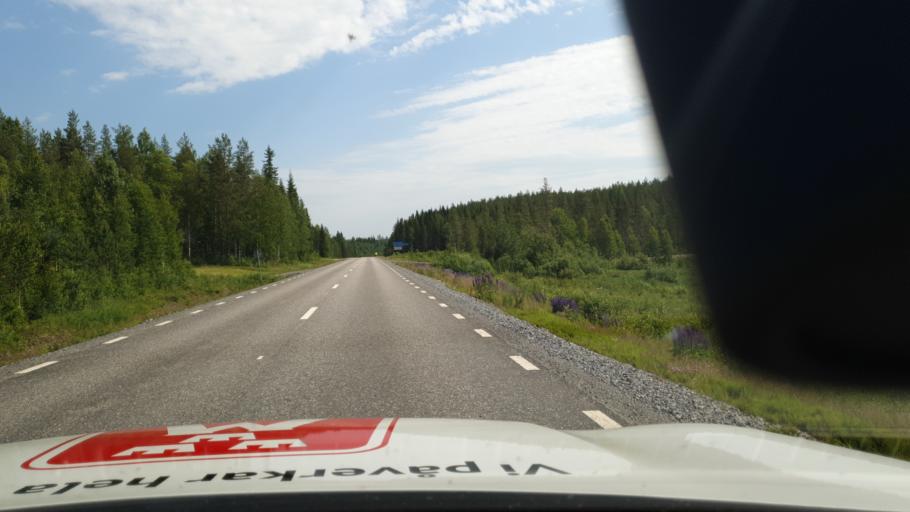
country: SE
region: Vaesterbotten
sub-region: Vindelns Kommun
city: Vindeln
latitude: 64.2543
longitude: 19.9496
